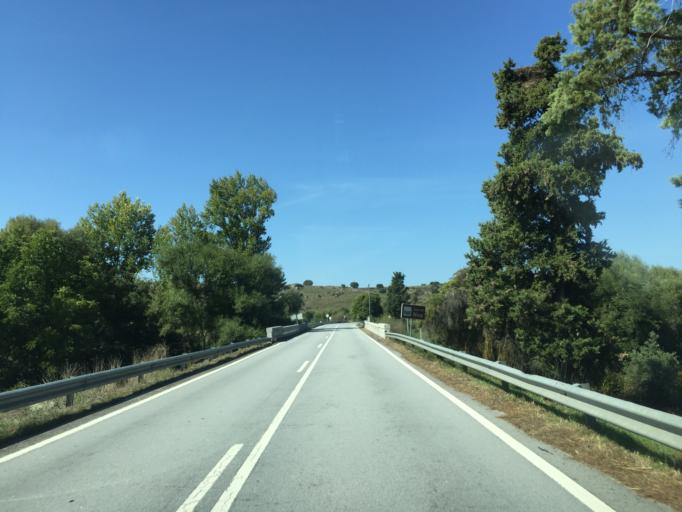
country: PT
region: Portalegre
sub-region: Portalegre
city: Alagoa
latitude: 39.4344
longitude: -7.5358
